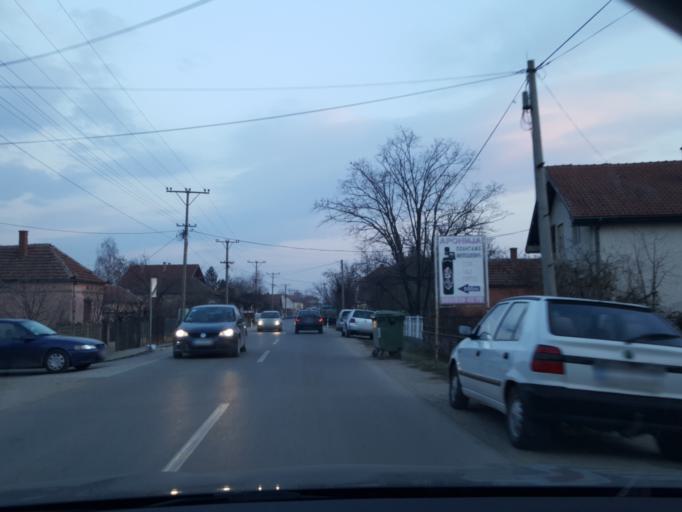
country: RS
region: Central Serbia
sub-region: Nisavski Okrug
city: Aleksinac
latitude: 43.5030
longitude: 21.7003
